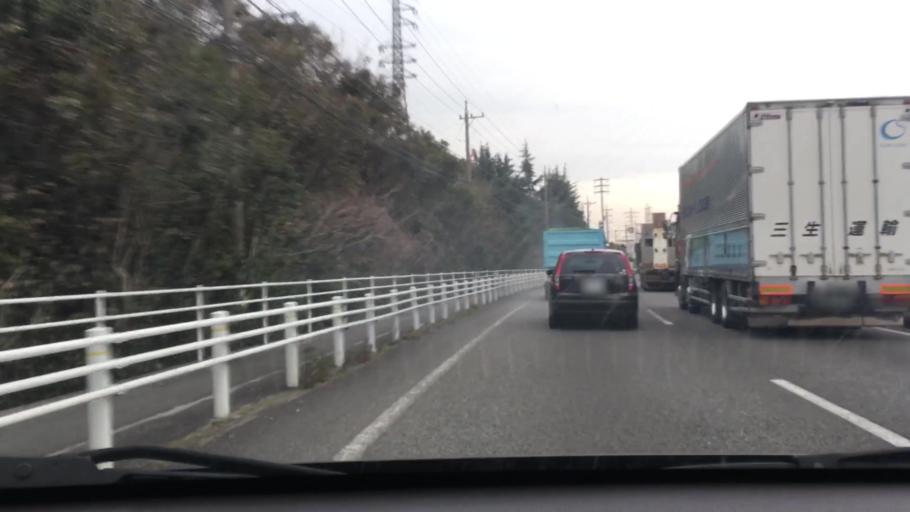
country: JP
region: Mie
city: Yokkaichi
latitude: 34.9357
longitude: 136.6152
